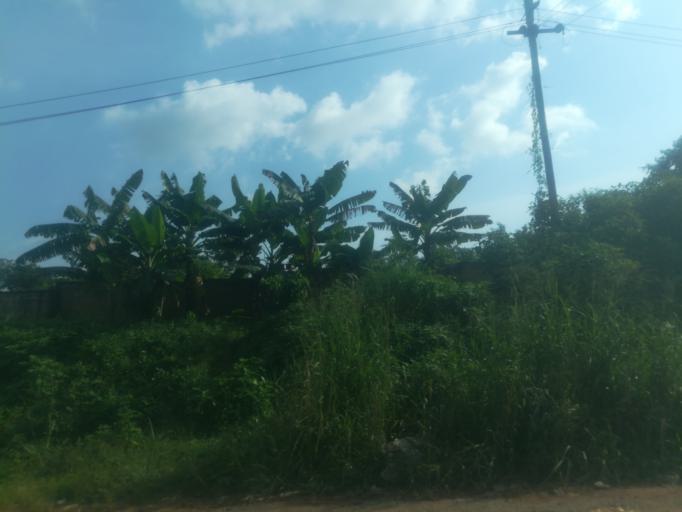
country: NG
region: Oyo
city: Ido
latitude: 7.3962
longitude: 3.7883
